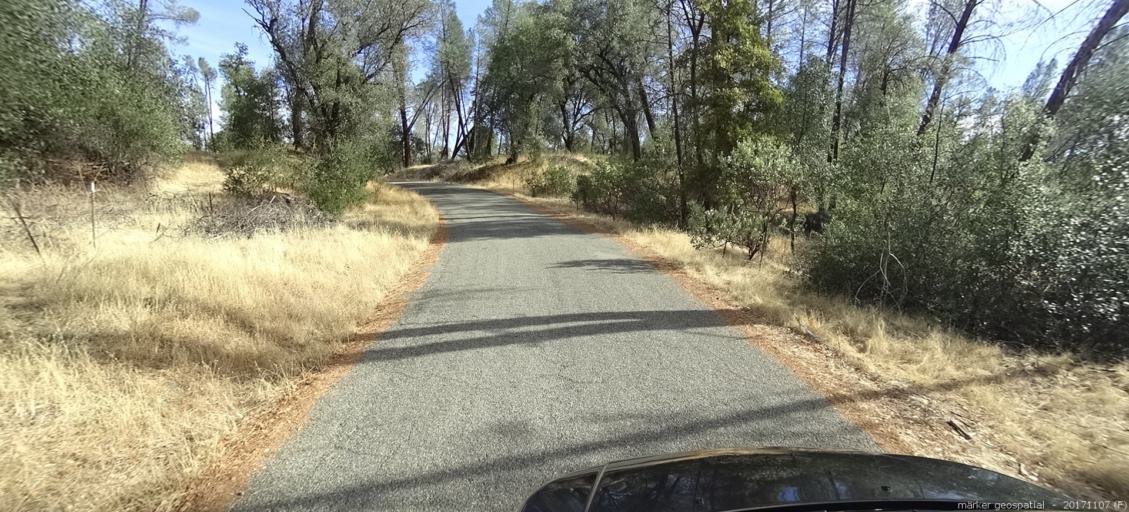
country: US
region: California
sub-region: Shasta County
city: Shasta
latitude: 40.4148
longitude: -122.5313
